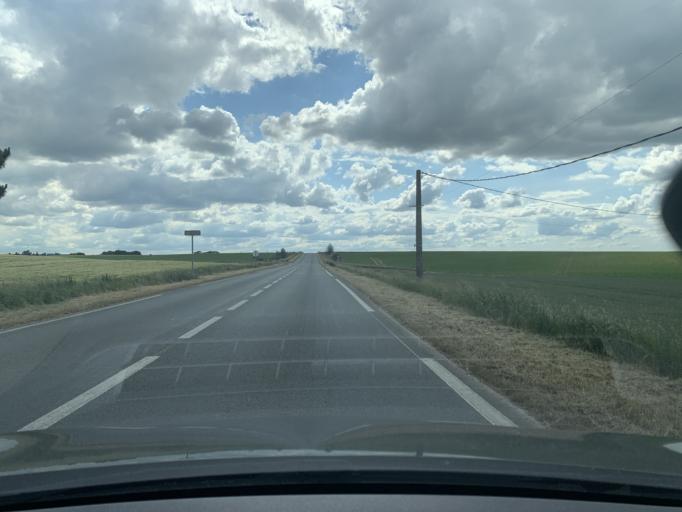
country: FR
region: Nord-Pas-de-Calais
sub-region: Departement du Nord
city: Gouzeaucourt
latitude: 50.0677
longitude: 3.1612
